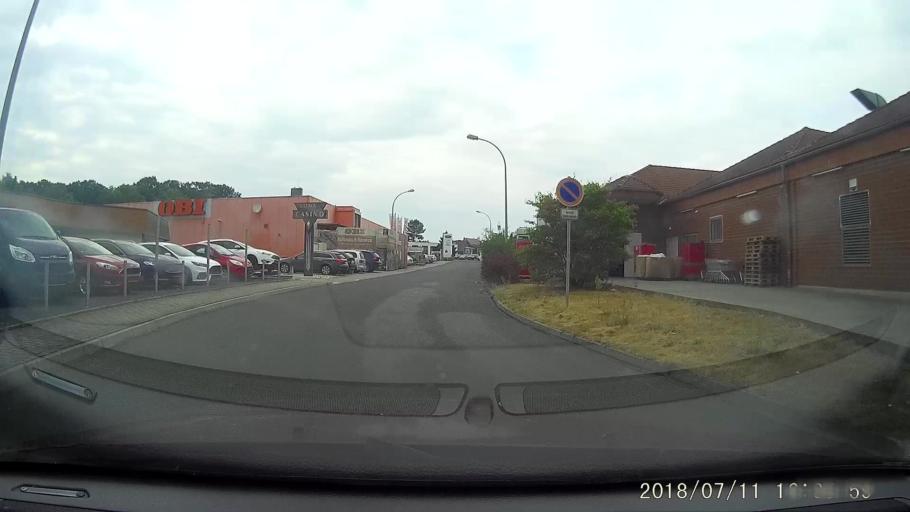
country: DE
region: Saxony
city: Niesky
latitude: 51.2866
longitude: 14.8190
